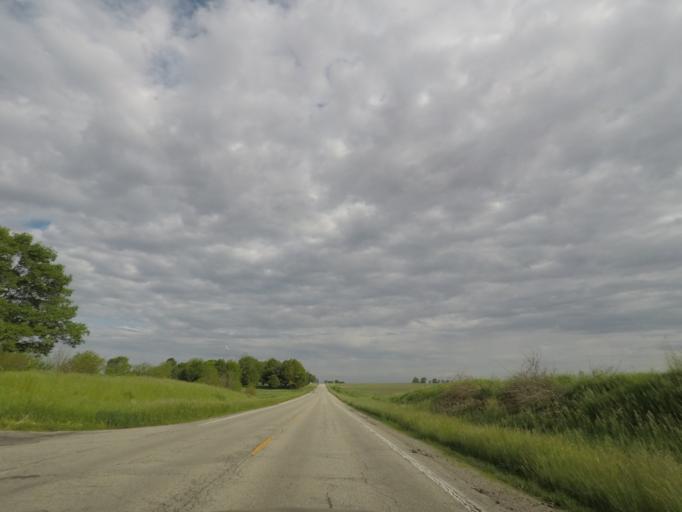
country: US
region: Illinois
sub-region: Logan County
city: Mount Pulaski
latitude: 40.0671
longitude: -89.2887
